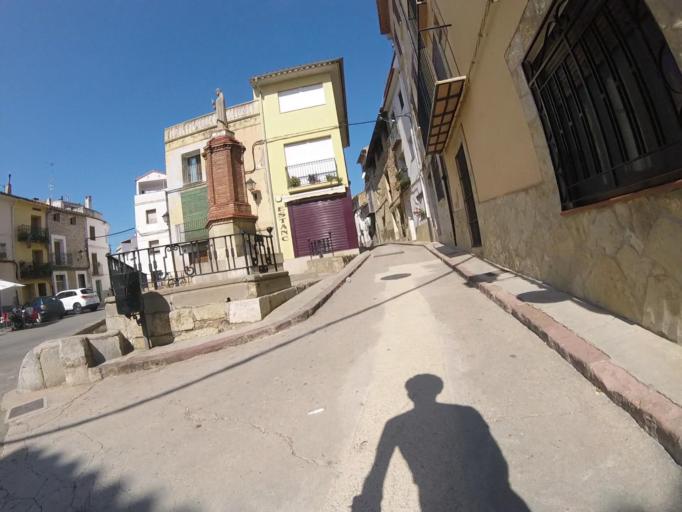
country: ES
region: Valencia
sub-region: Provincia de Castello
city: Adzaneta
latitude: 40.2164
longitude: -0.1707
